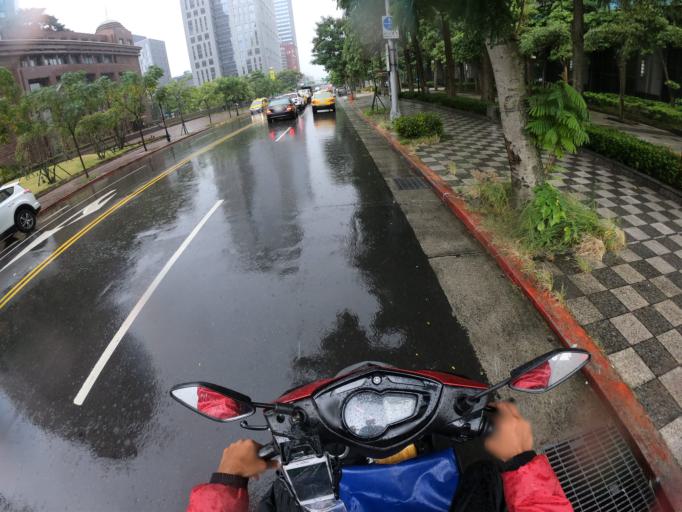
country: TW
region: Taipei
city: Taipei
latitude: 25.0391
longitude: 121.5697
